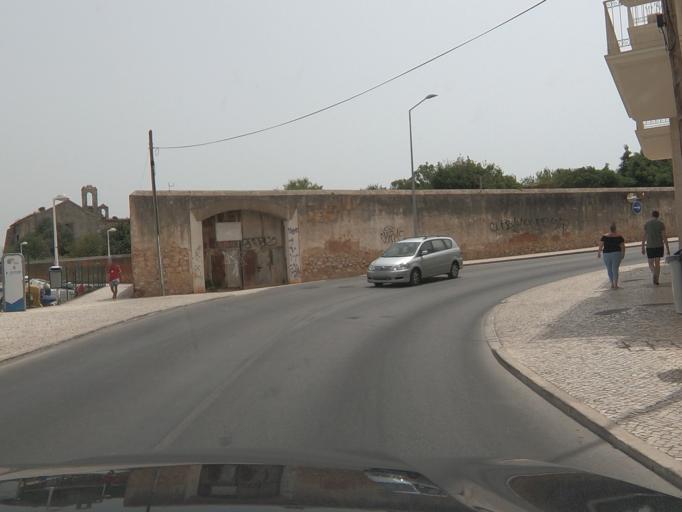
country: PT
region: Faro
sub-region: Portimao
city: Portimao
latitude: 37.1295
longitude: -8.5336
